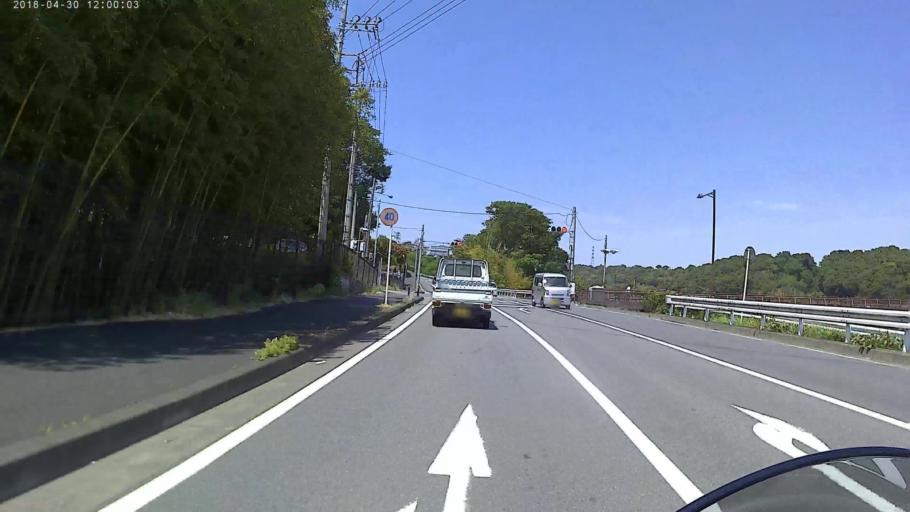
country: JP
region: Kanagawa
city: Zama
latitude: 35.5115
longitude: 139.3284
